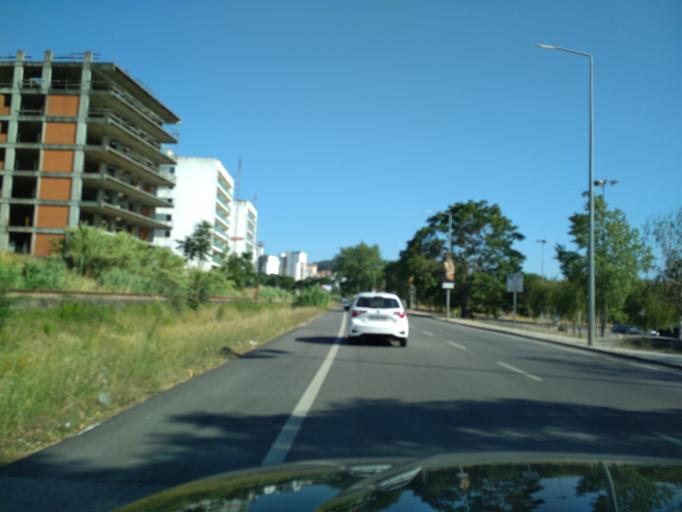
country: PT
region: Coimbra
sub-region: Coimbra
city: Coimbra
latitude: 40.2010
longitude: -8.4239
